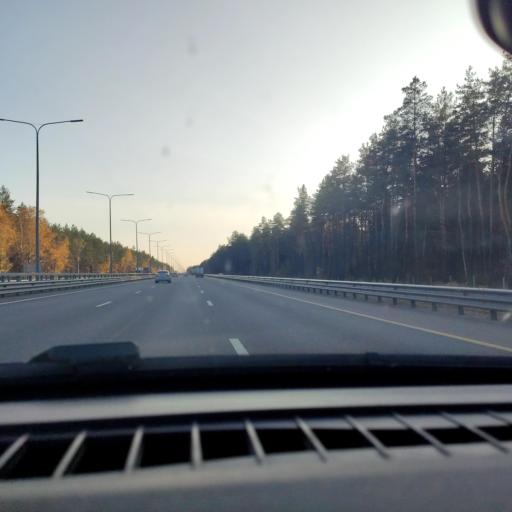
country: RU
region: Voronezj
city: Somovo
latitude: 51.7243
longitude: 39.3104
